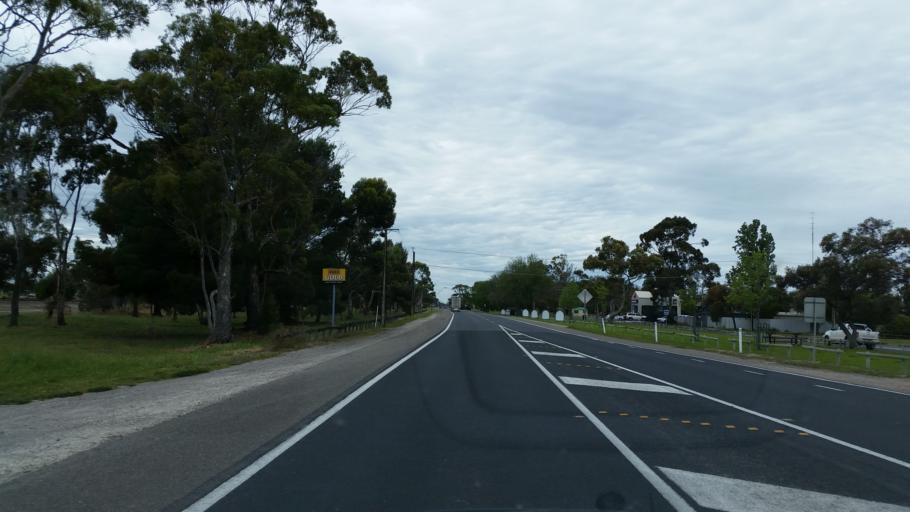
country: AU
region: South Australia
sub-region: Tatiara
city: Keith
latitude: -36.0982
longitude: 140.3552
